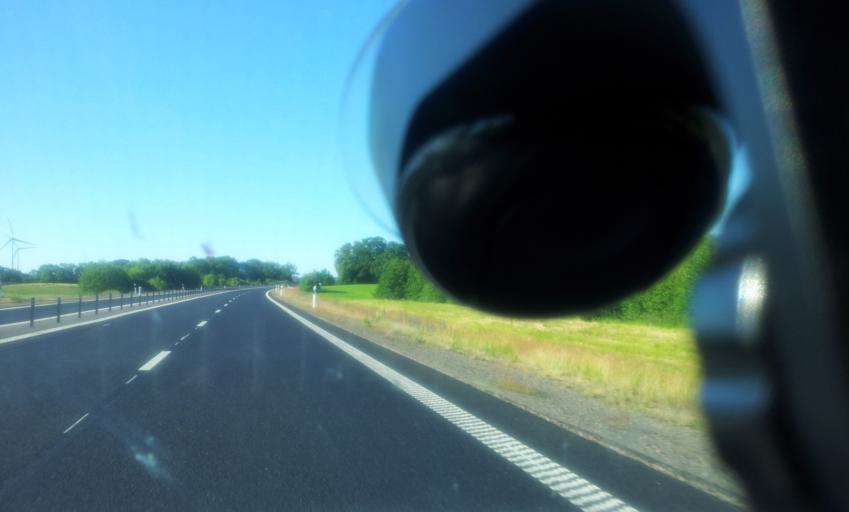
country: SE
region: Kalmar
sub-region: Torsas Kommun
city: Torsas
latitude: 56.4468
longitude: 16.0791
